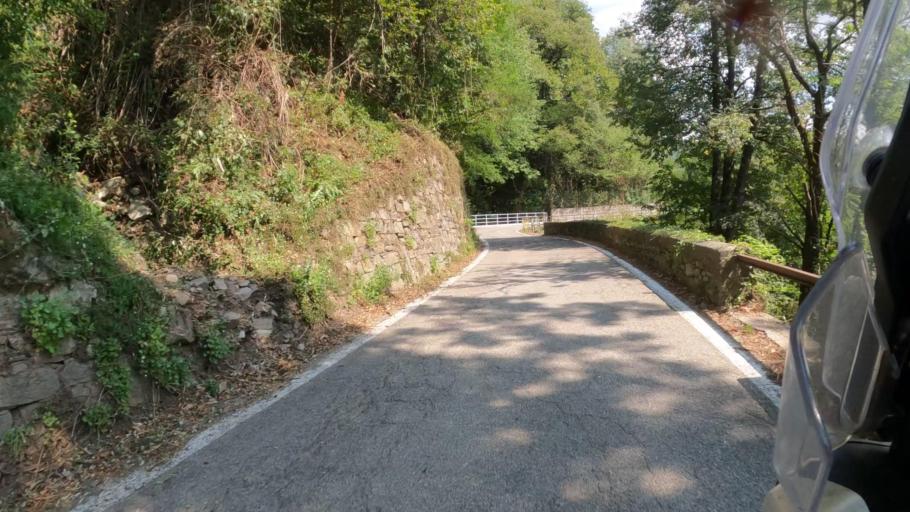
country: IT
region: Lombardy
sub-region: Provincia di Varese
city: Agra
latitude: 46.0572
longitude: 8.7675
